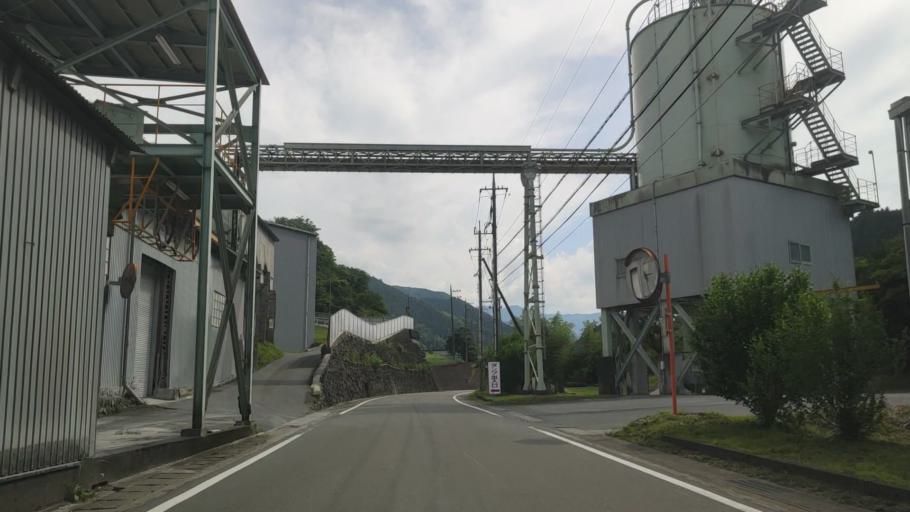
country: JP
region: Gunma
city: Tomioka
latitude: 36.1866
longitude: 138.7488
